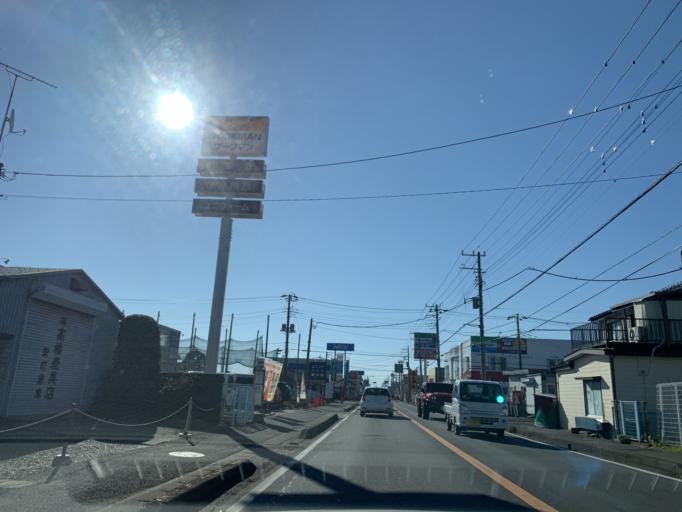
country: JP
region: Chiba
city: Matsudo
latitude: 35.8131
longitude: 139.8953
